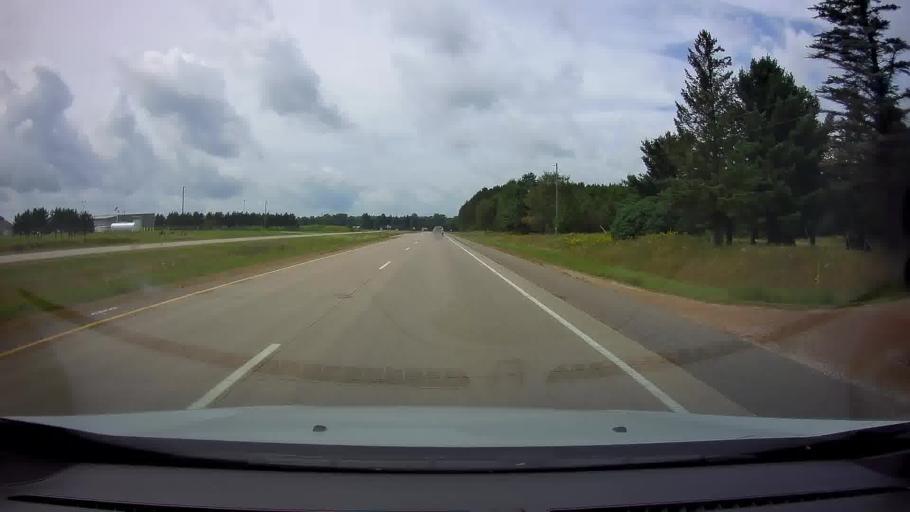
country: US
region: Wisconsin
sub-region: Shawano County
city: Wittenberg
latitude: 44.8039
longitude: -89.0242
